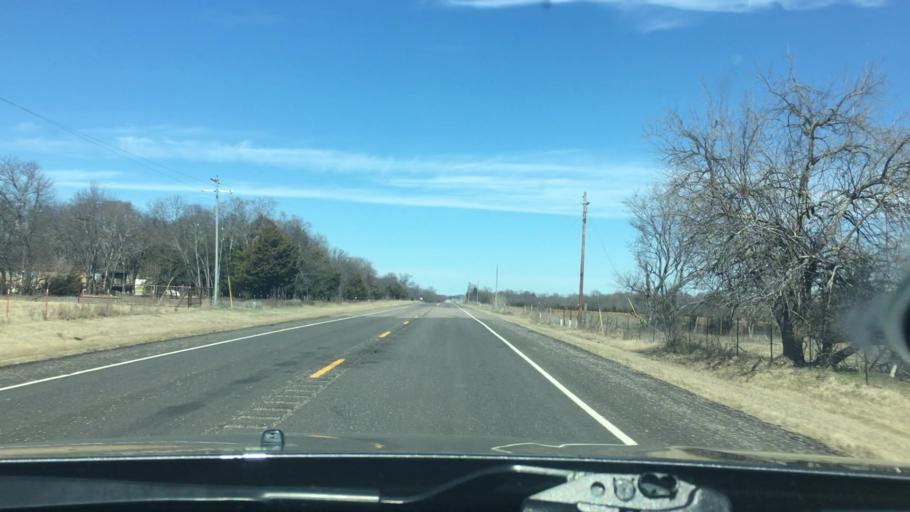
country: US
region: Oklahoma
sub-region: Murray County
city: Sulphur
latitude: 34.3537
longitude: -96.9509
